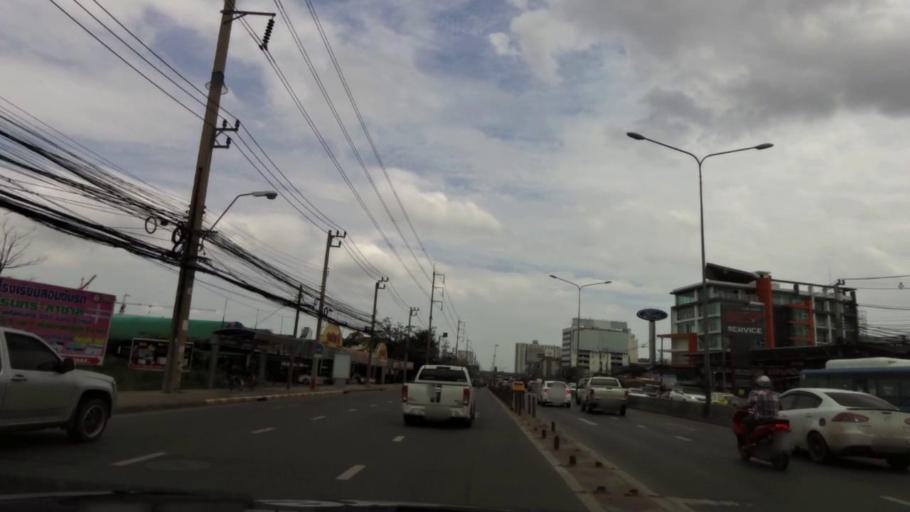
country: TH
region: Bangkok
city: Bang Na
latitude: 13.6818
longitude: 100.6465
